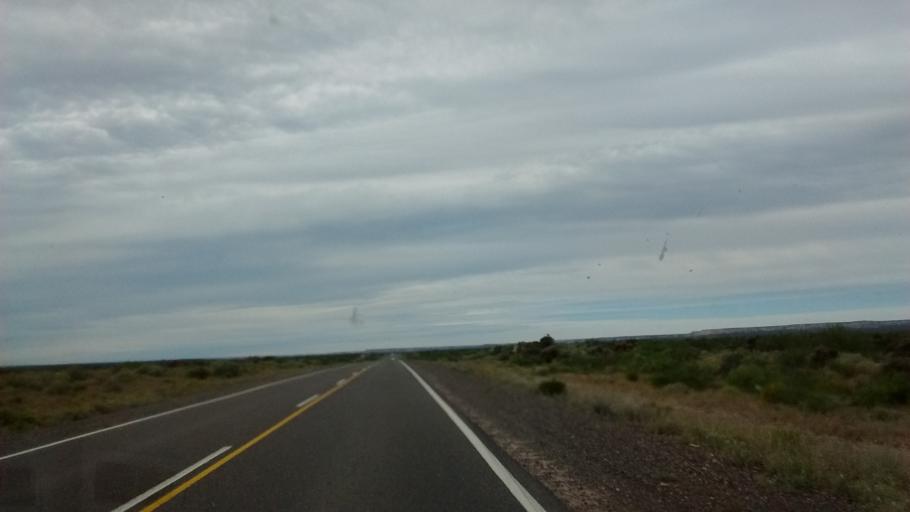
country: AR
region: Rio Negro
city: Catriel
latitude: -38.0892
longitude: -67.9261
